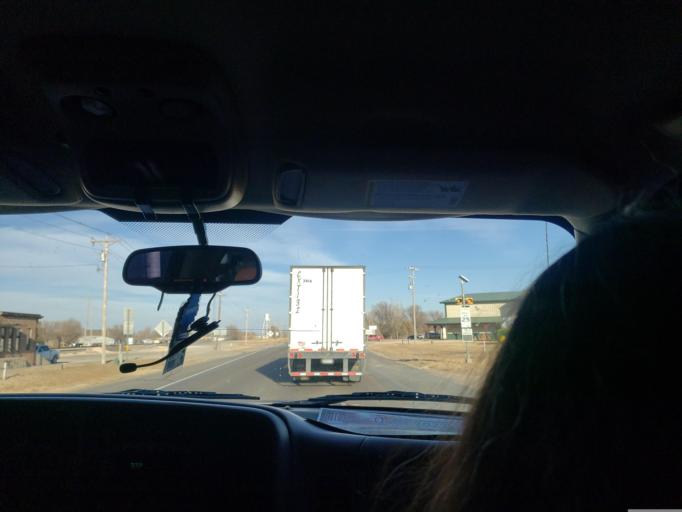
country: US
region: Oklahoma
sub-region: Texas County
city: Goodwell
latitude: 36.4994
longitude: -101.7887
